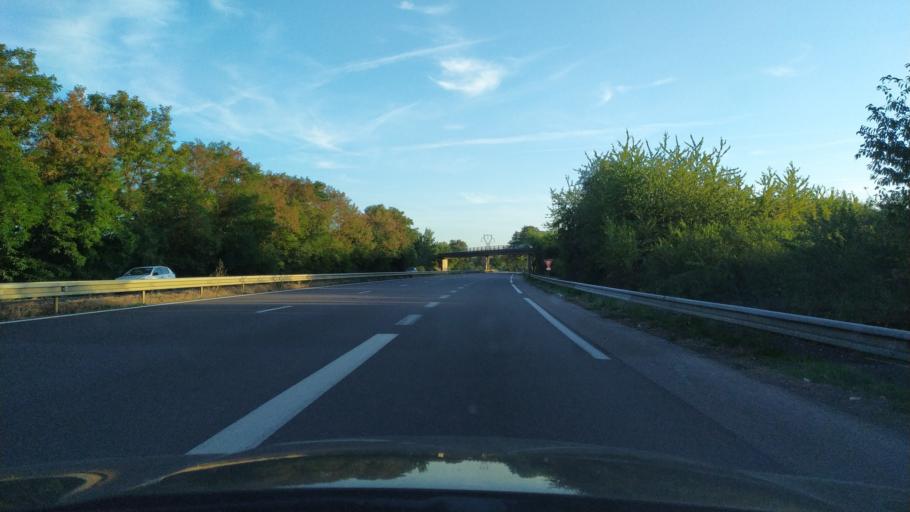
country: FR
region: Lorraine
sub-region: Departement de la Moselle
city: Maizieres-les-Metz
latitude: 49.2085
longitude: 6.1497
